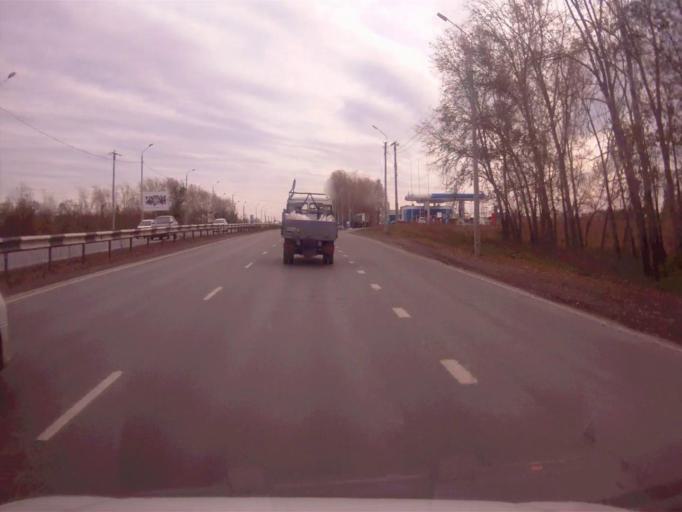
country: RU
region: Chelyabinsk
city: Novosineglazovskiy
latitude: 55.0562
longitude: 61.4065
